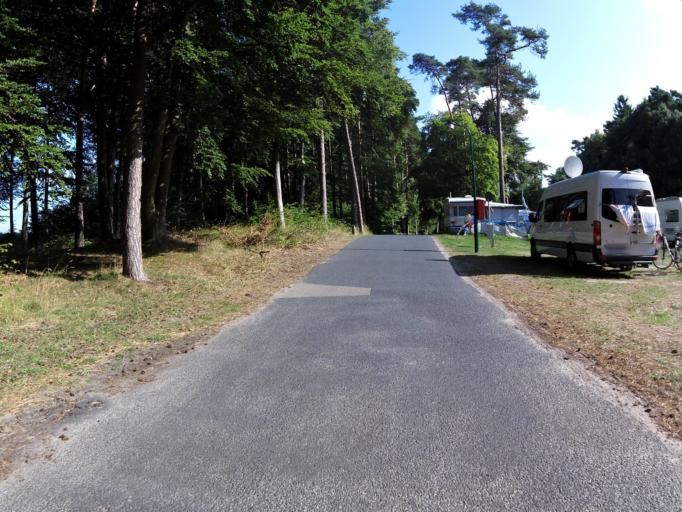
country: DE
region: Mecklenburg-Vorpommern
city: Seebad Bansin
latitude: 53.9984
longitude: 14.1024
